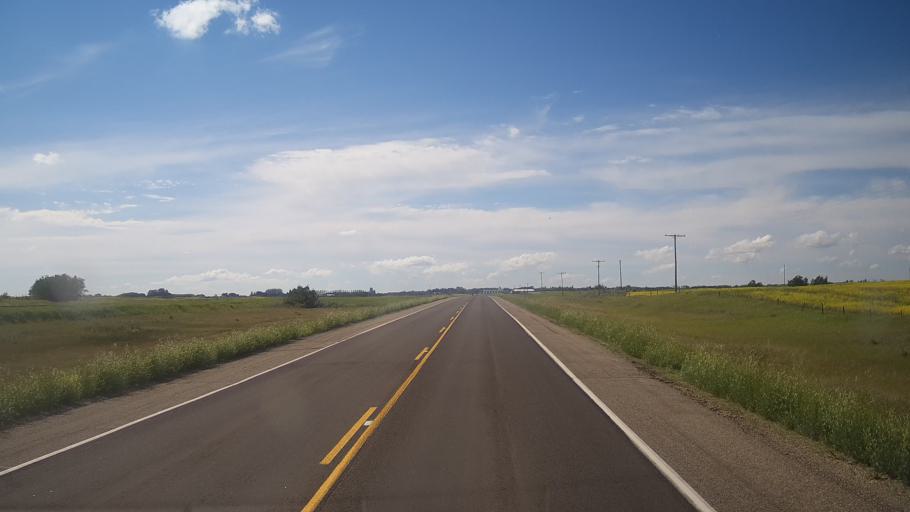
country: CA
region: Saskatchewan
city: Foam Lake
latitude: 51.2505
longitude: -103.7026
